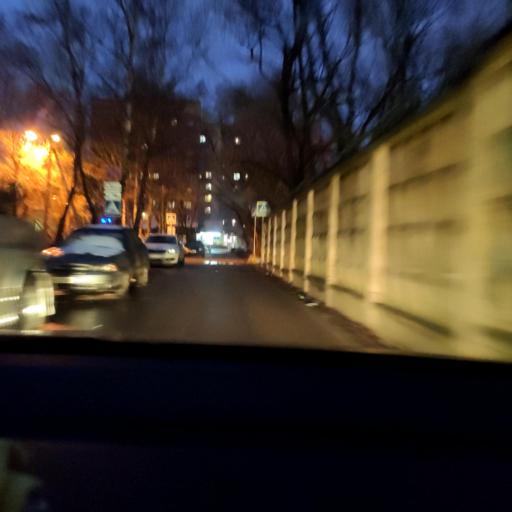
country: RU
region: Moskovskaya
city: Lesnoy Gorodok
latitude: 55.6580
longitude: 37.2062
